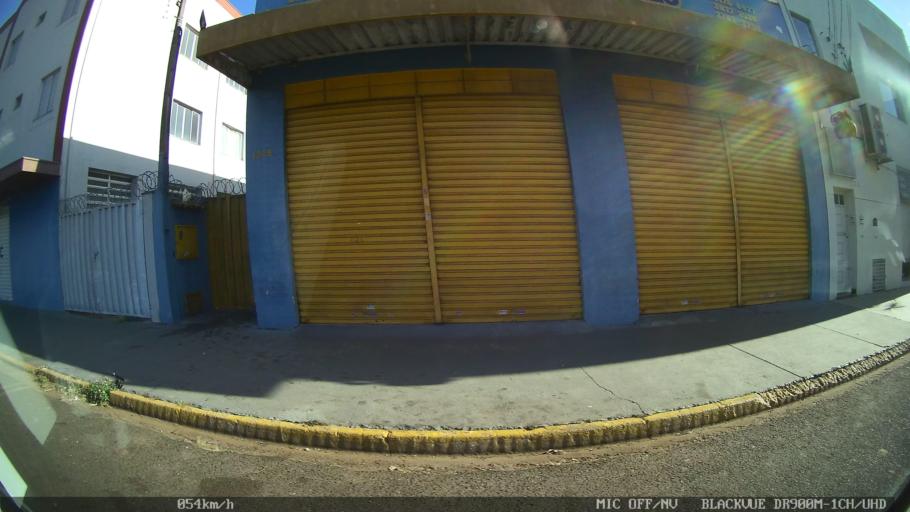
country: BR
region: Sao Paulo
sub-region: Franca
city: Franca
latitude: -20.5102
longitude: -47.3913
